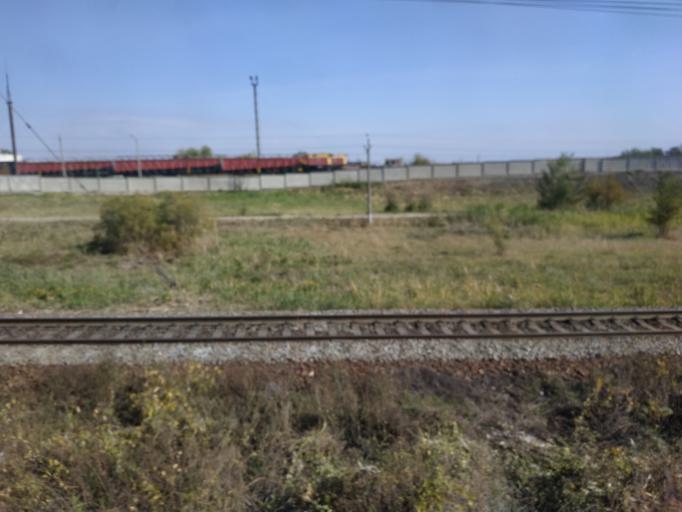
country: RU
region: Volgograd
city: Volgograd
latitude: 48.7676
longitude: 44.5122
